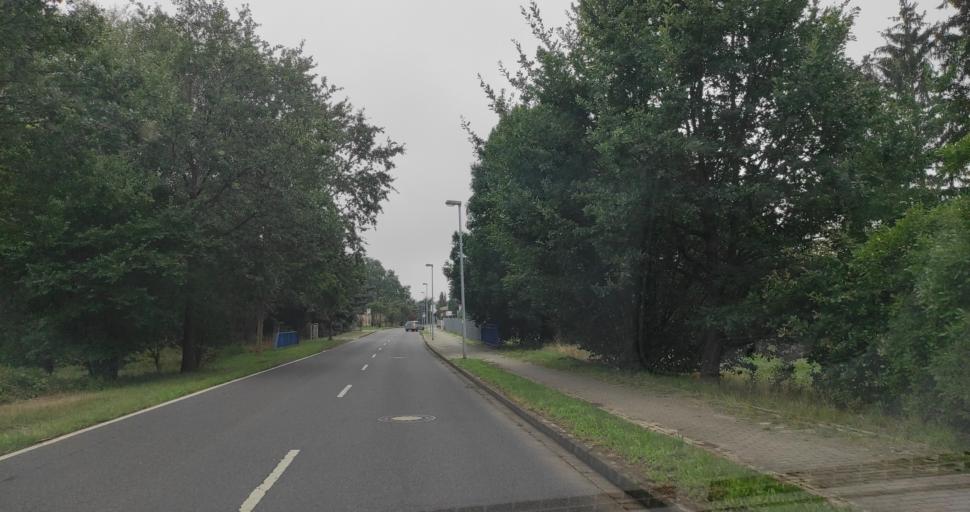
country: DE
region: Brandenburg
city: Forst
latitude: 51.7130
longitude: 14.6291
